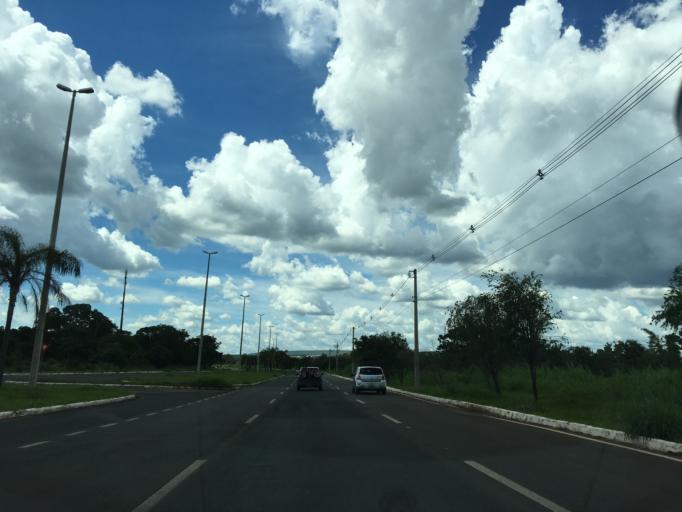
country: BR
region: Federal District
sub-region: Brasilia
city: Brasilia
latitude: -15.7529
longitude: -47.8773
